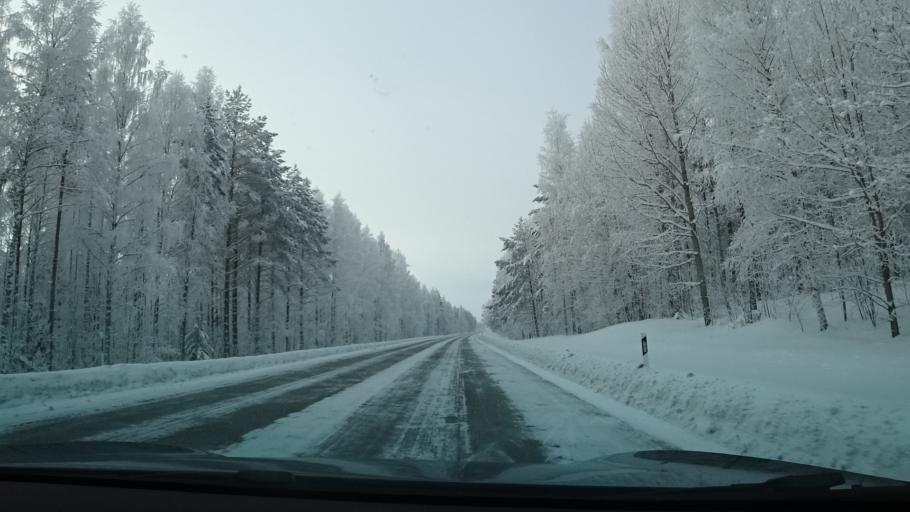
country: FI
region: South Karelia
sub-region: Imatra
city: Saari
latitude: 61.7832
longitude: 29.7123
